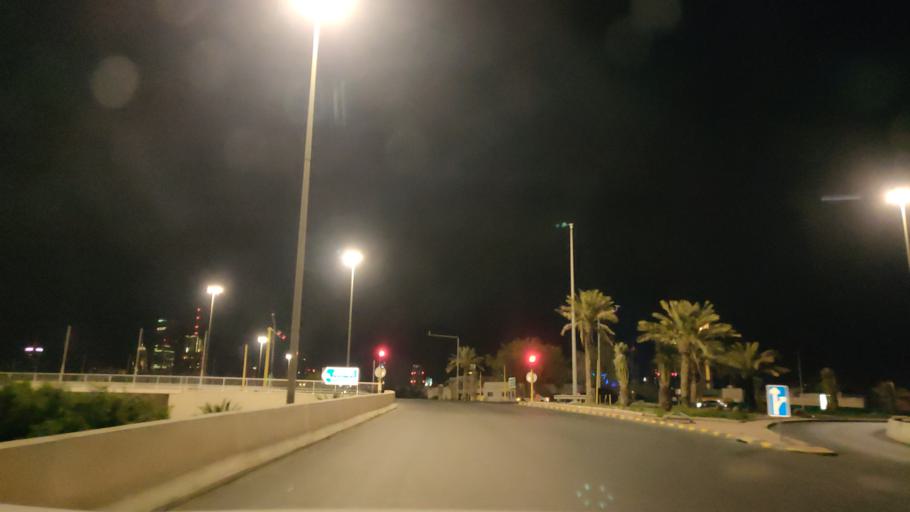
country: KW
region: Al Asimah
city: Ad Dasmah
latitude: 29.3499
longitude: 47.9948
